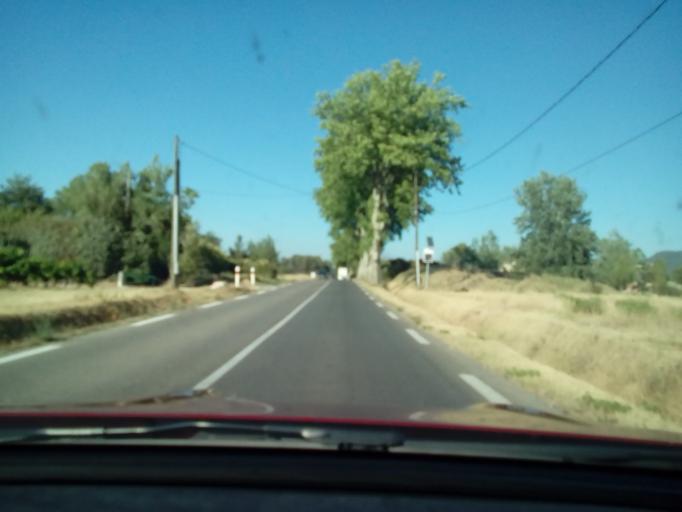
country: FR
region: Provence-Alpes-Cote d'Azur
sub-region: Departement des Bouches-du-Rhone
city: Trets
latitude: 43.4532
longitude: 5.6981
